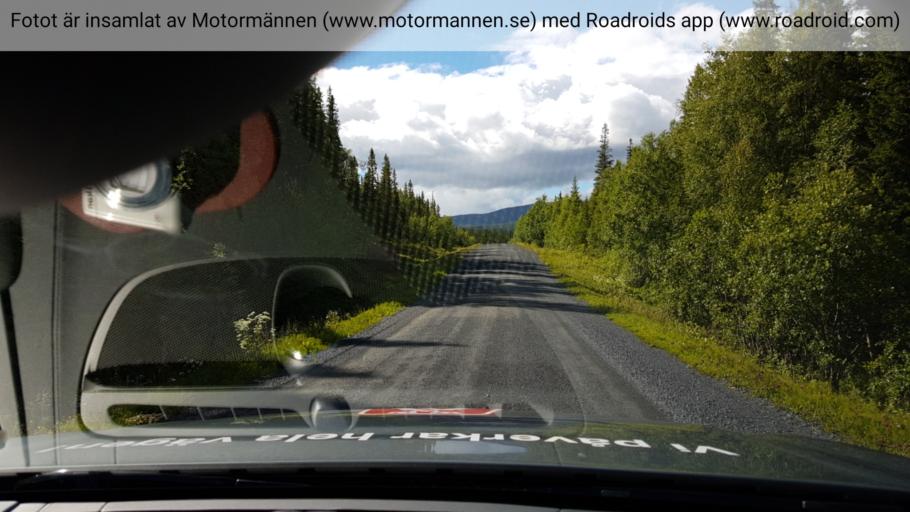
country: SE
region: Jaemtland
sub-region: Krokoms Kommun
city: Valla
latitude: 63.0981
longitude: 13.8873
